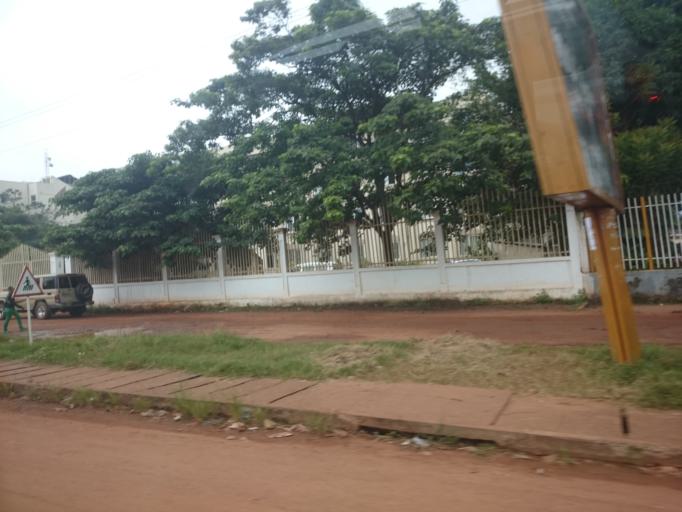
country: CF
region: Bangui
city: Bangui
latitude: 4.3648
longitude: 18.5672
